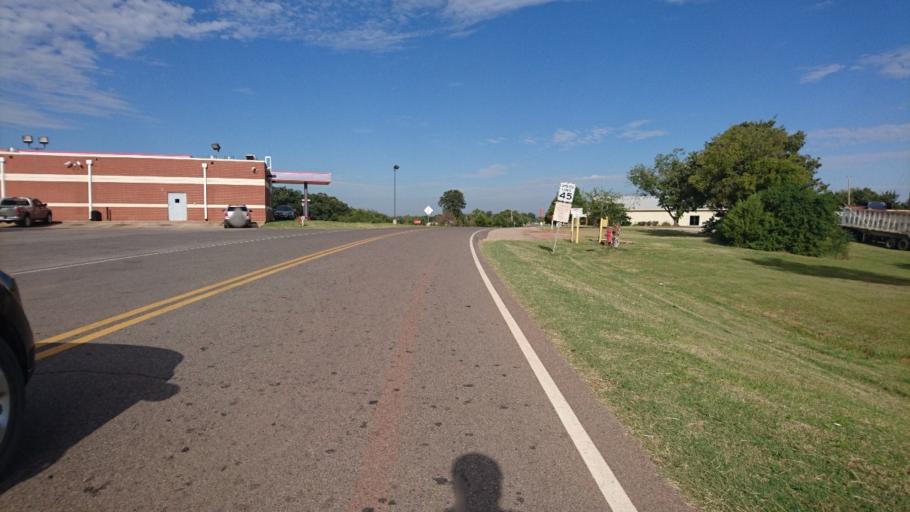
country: US
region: Oklahoma
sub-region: Oklahoma County
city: Luther
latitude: 35.6814
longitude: -97.0540
